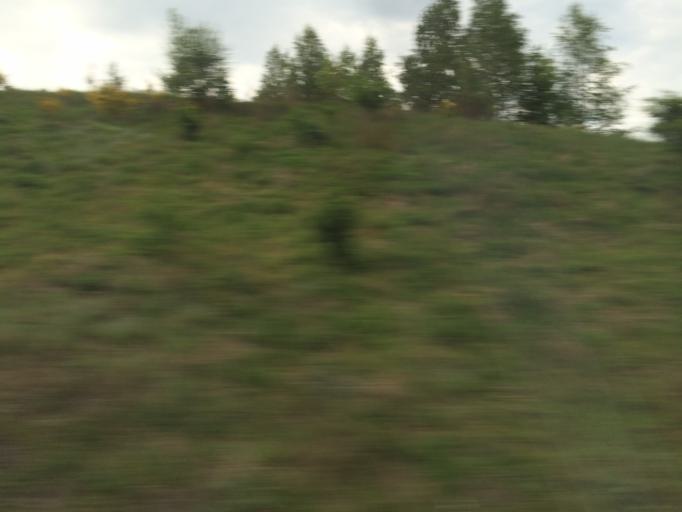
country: DE
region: Rheinland-Pfalz
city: Montabaur
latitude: 50.4449
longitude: 7.8173
